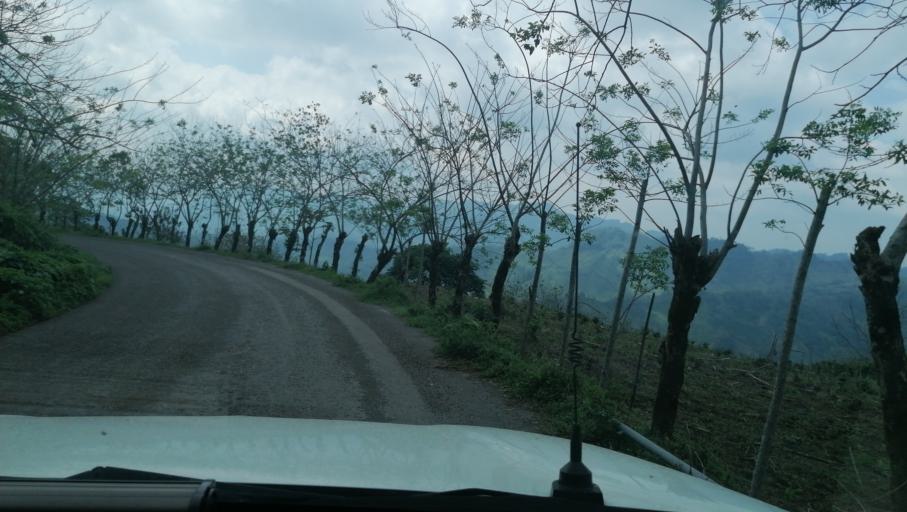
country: MX
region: Chiapas
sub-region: Francisco Leon
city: San Miguel la Sardina
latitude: 17.2434
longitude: -93.2966
